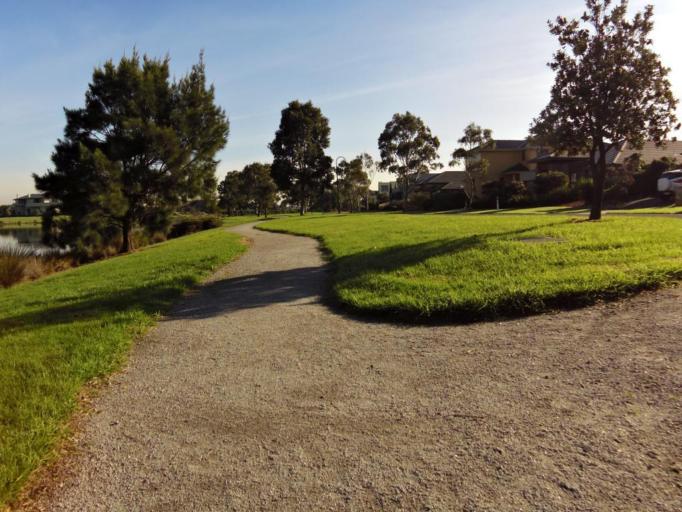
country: AU
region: Victoria
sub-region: Kingston
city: Waterways
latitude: -38.0188
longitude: 145.1378
